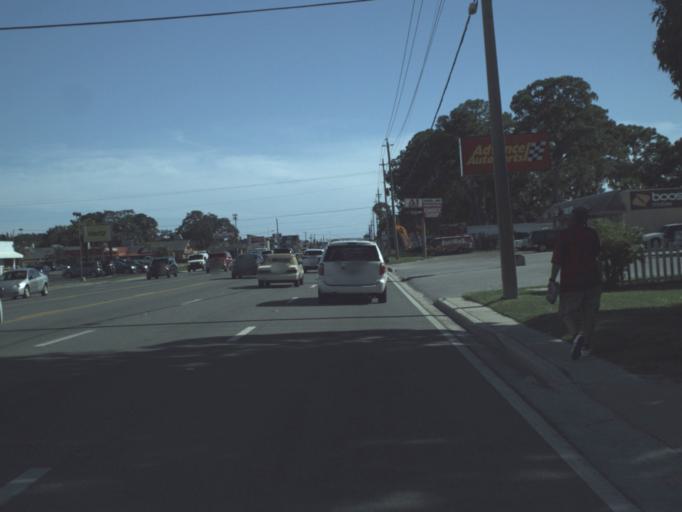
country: US
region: Florida
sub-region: Manatee County
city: South Bradenton
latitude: 27.4535
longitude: -82.5755
